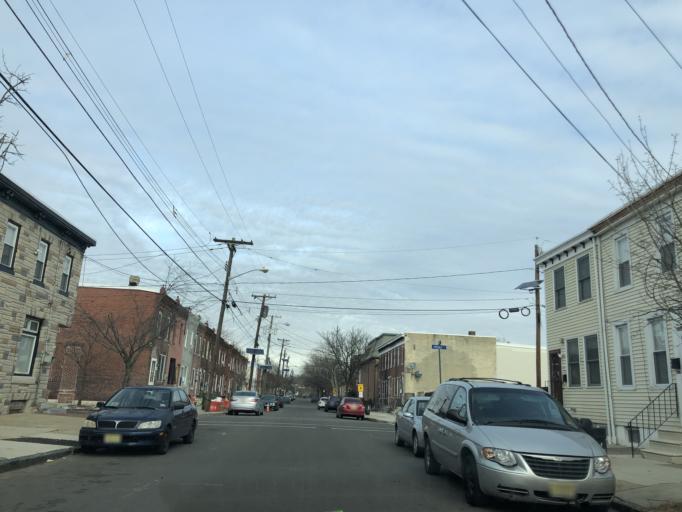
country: US
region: New Jersey
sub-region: Camden County
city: Camden
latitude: 39.9212
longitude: -75.1215
